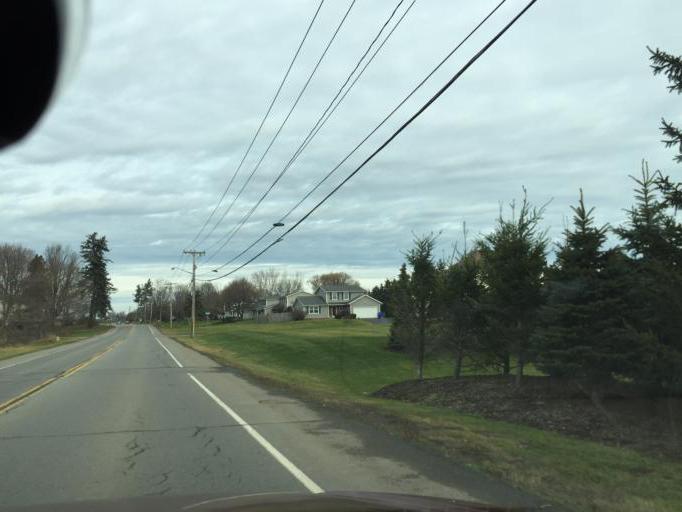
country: US
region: New York
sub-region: Monroe County
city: Scottsville
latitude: 43.1003
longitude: -77.7324
